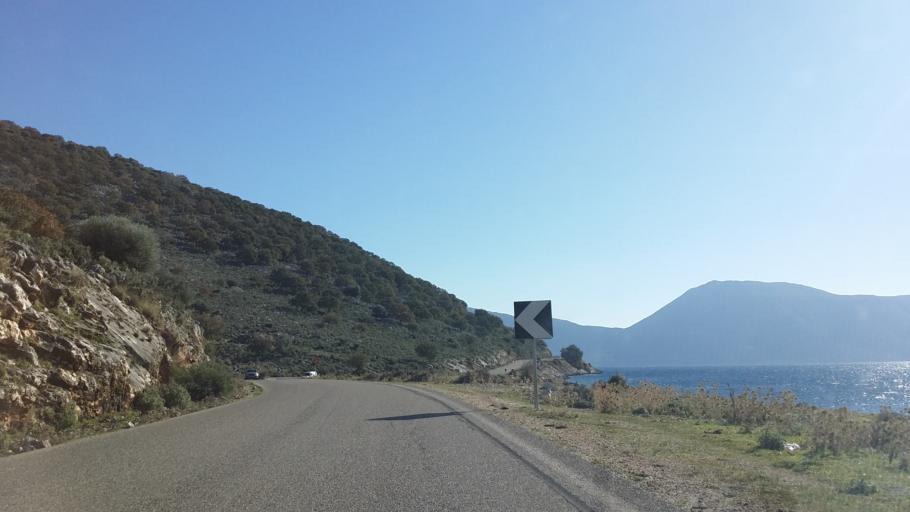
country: GR
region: West Greece
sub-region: Nomos Aitolias kai Akarnanias
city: Kandila
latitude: 38.7054
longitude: 20.8965
